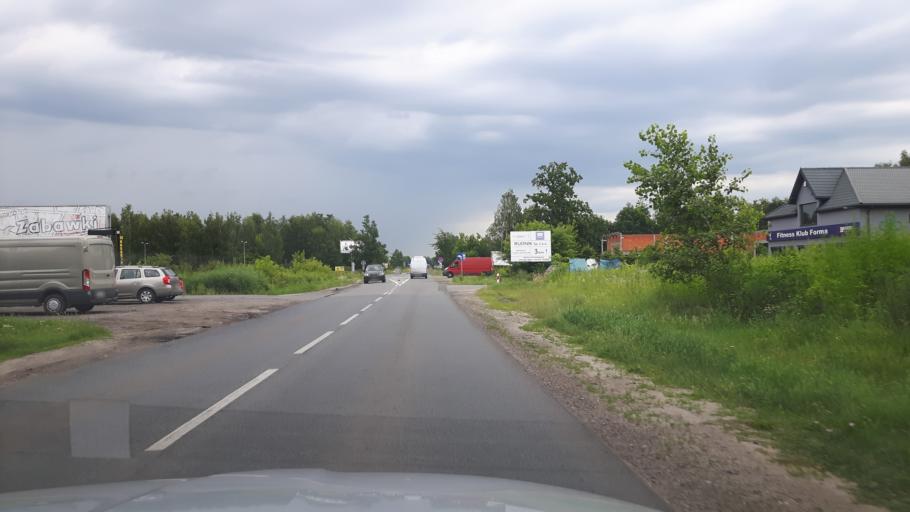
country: PL
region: Masovian Voivodeship
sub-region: Powiat wolominski
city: Wolomin
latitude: 52.3419
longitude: 21.2582
